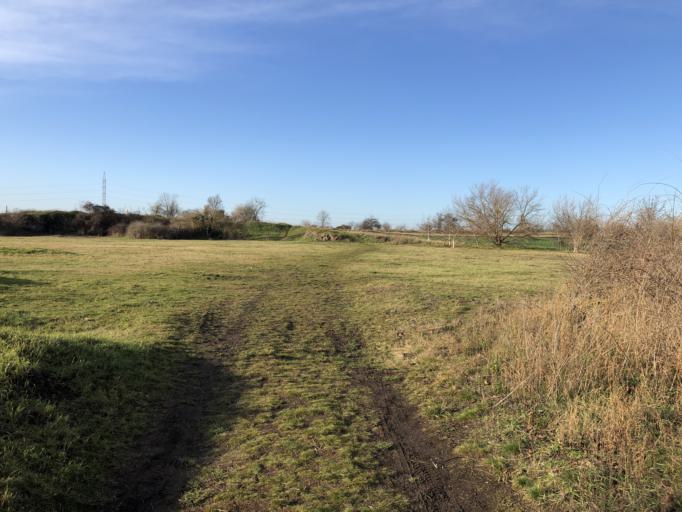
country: DE
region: Saxony-Anhalt
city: Halle (Saale)
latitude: 51.4911
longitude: 12.0233
